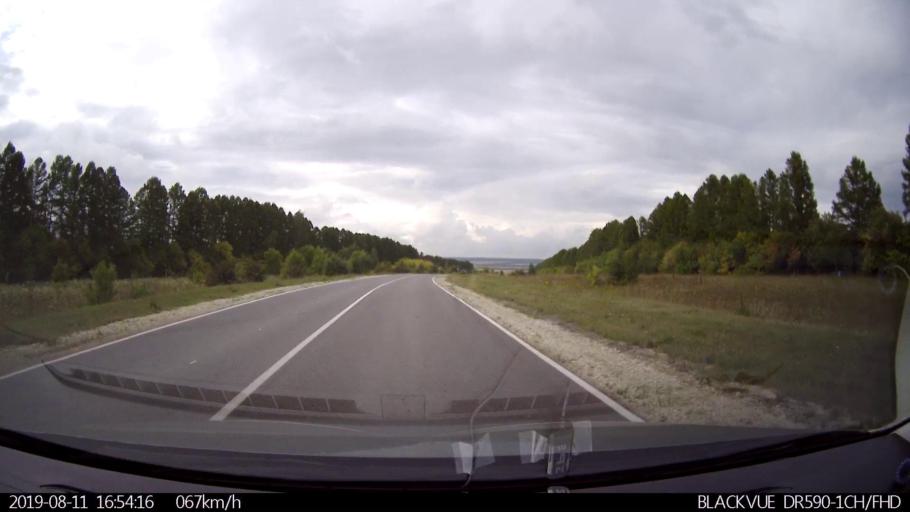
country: RU
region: Ulyanovsk
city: Mayna
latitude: 54.2709
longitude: 47.6665
